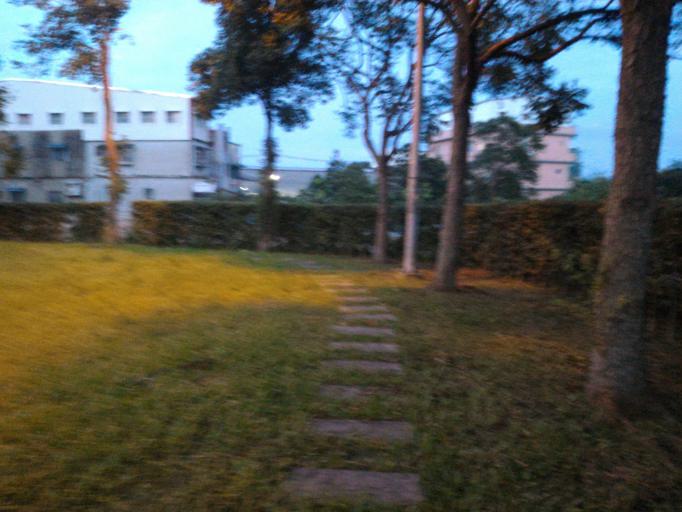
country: TW
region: Taipei
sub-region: Taipei
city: Banqiao
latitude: 24.9614
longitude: 121.4006
